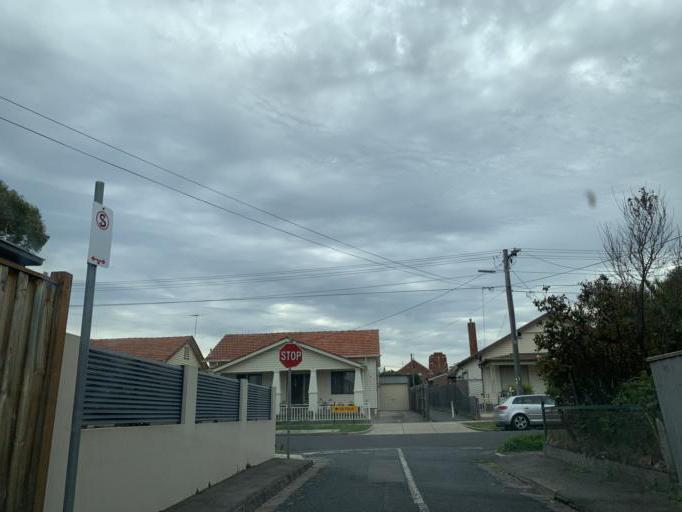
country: AU
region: Victoria
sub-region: Moreland
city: Coburg
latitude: -37.7482
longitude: 144.9742
